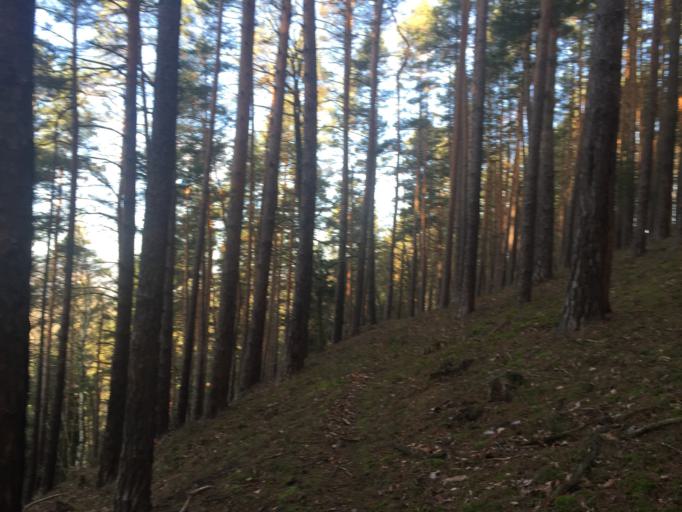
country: DE
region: Thuringia
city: Freienorla
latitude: 50.7567
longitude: 11.5362
